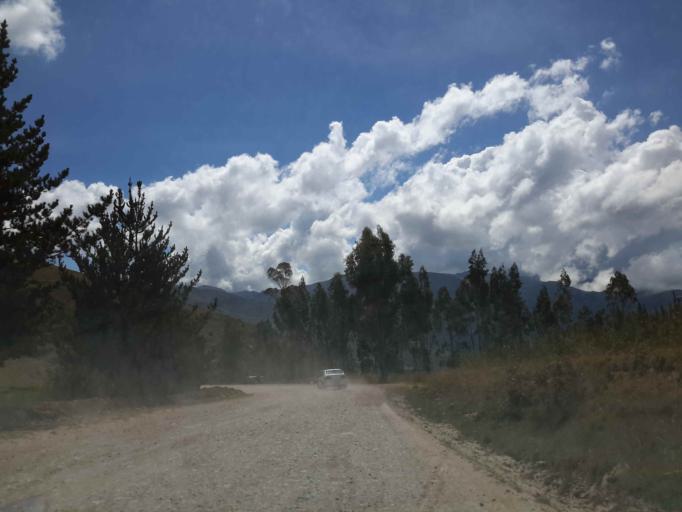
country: PE
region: Apurimac
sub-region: Provincia de Andahuaylas
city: Pacucha
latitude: -13.6302
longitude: -73.3386
